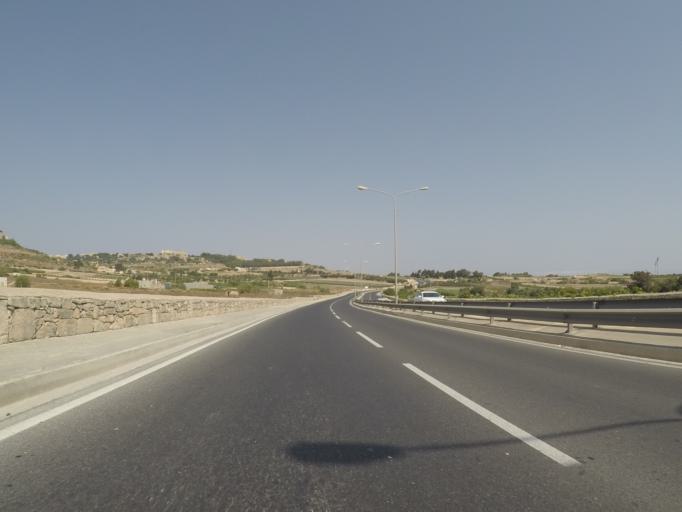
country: MT
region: L-Imdina
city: Imdina
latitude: 35.8858
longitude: 14.4114
